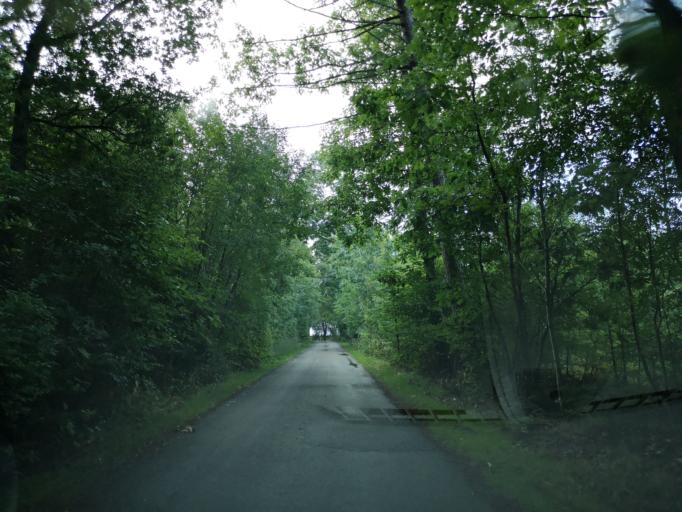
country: DK
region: Central Jutland
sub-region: Holstebro Kommune
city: Holstebro
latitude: 56.3355
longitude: 8.6381
